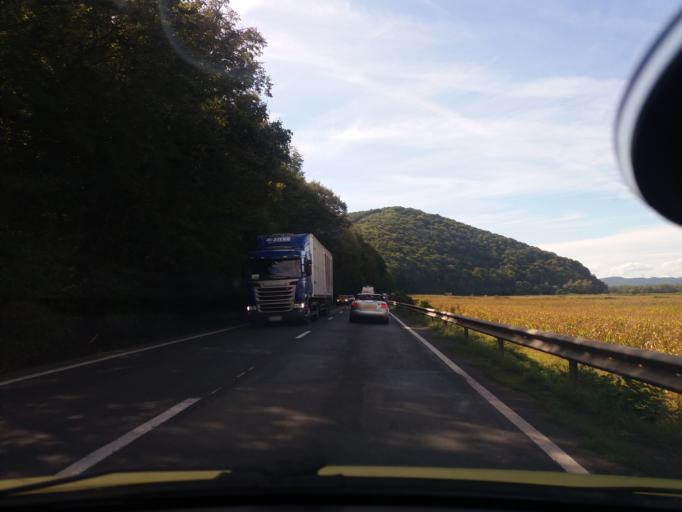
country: RO
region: Hunedoara
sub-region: Comuna Ilia
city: Ilia
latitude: 45.9202
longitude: 22.7132
